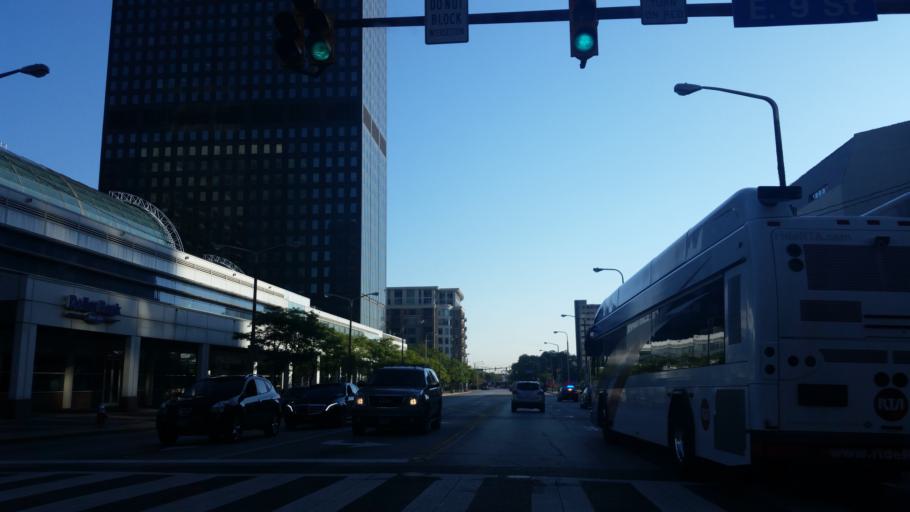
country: US
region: Ohio
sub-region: Cuyahoga County
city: Cleveland
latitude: 41.5039
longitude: -81.6900
